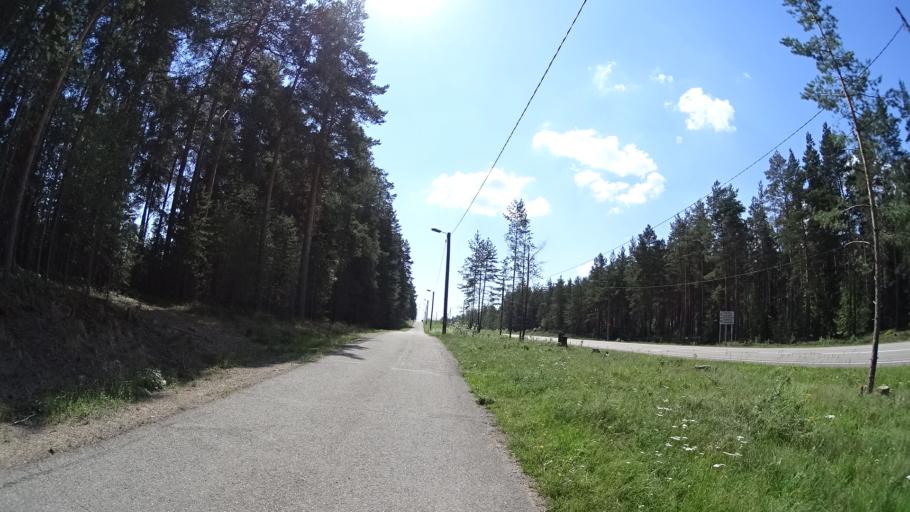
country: FI
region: Uusimaa
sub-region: Helsinki
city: Vantaa
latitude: 60.3182
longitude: 25.0005
